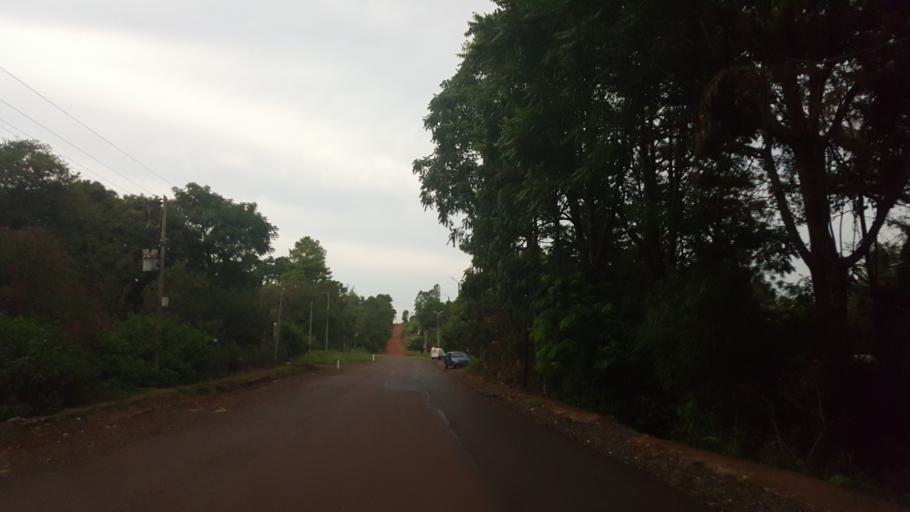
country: AR
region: Misiones
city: Puerto Leoni
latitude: -27.0054
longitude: -55.1640
